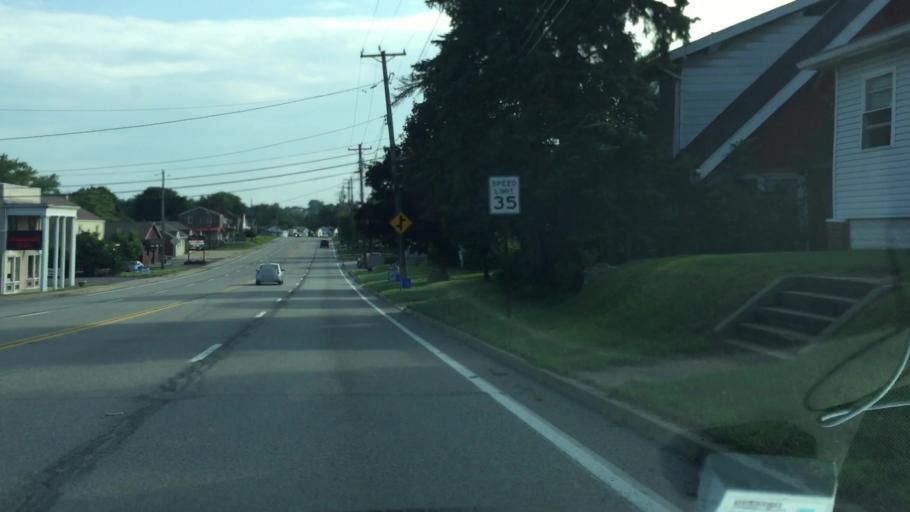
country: US
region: Pennsylvania
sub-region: Beaver County
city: Aliquippa
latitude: 40.6039
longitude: -80.2892
